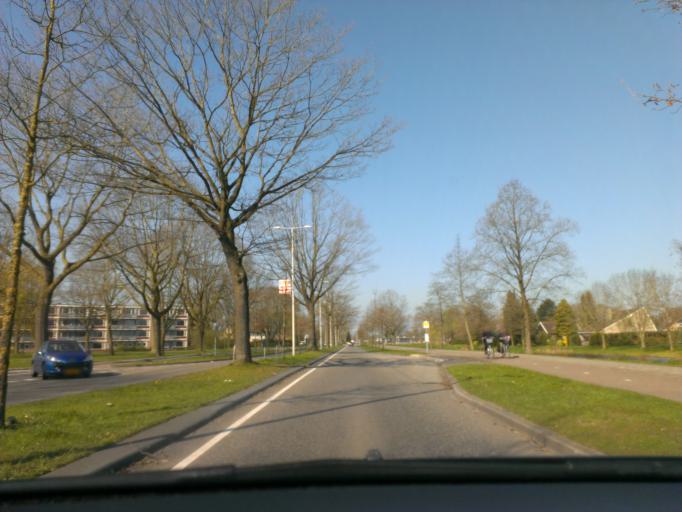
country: NL
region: Drenthe
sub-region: Gemeente Hoogeveen
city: Hoogeveen
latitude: 52.7207
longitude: 6.5063
